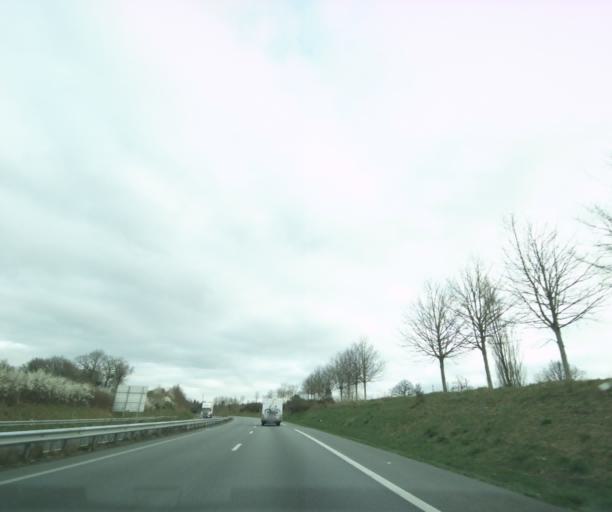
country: FR
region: Limousin
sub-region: Departement de la Haute-Vienne
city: Pierre-Buffiere
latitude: 45.6813
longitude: 1.3686
